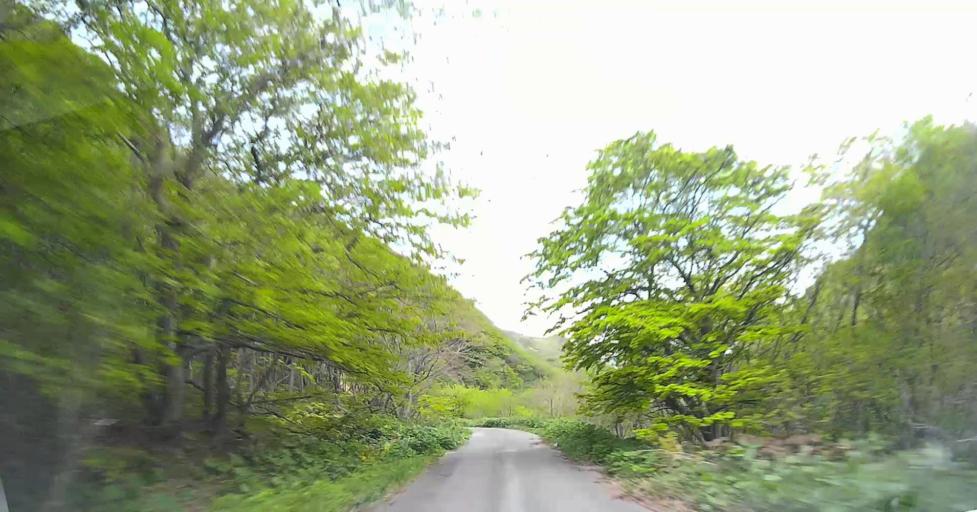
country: JP
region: Aomori
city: Shimokizukuri
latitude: 41.2376
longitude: 140.3450
